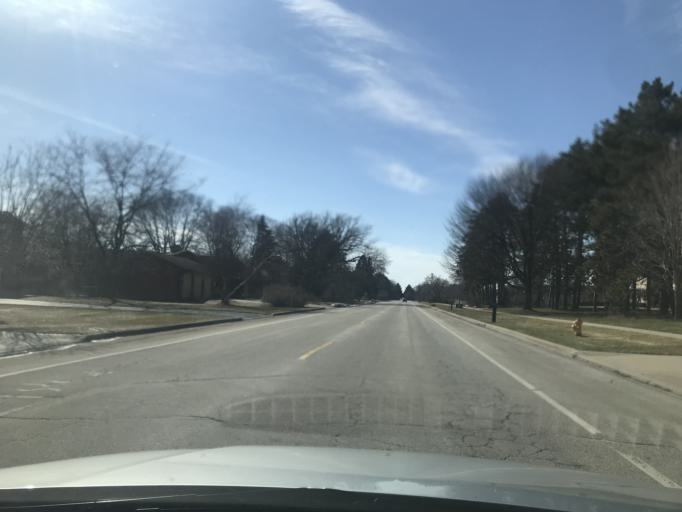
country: US
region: Wisconsin
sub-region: Marinette County
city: Marinette
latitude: 45.1118
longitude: -87.6430
